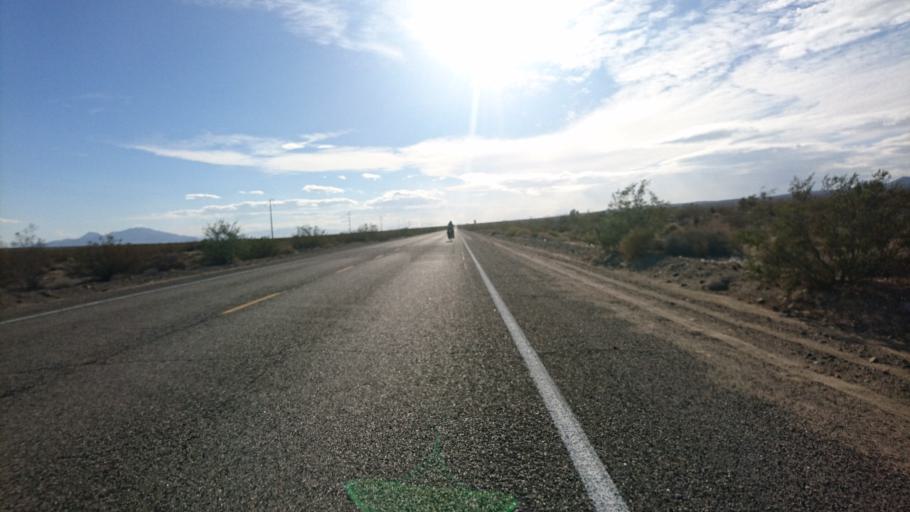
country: US
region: California
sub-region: San Bernardino County
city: Needles
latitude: 34.6939
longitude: -115.3073
